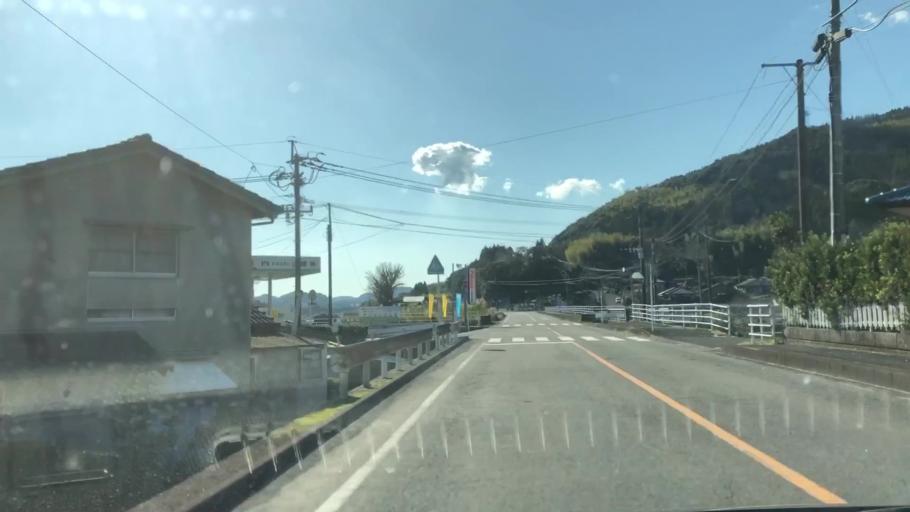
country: JP
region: Kagoshima
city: Satsumasendai
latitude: 31.8681
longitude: 130.4250
